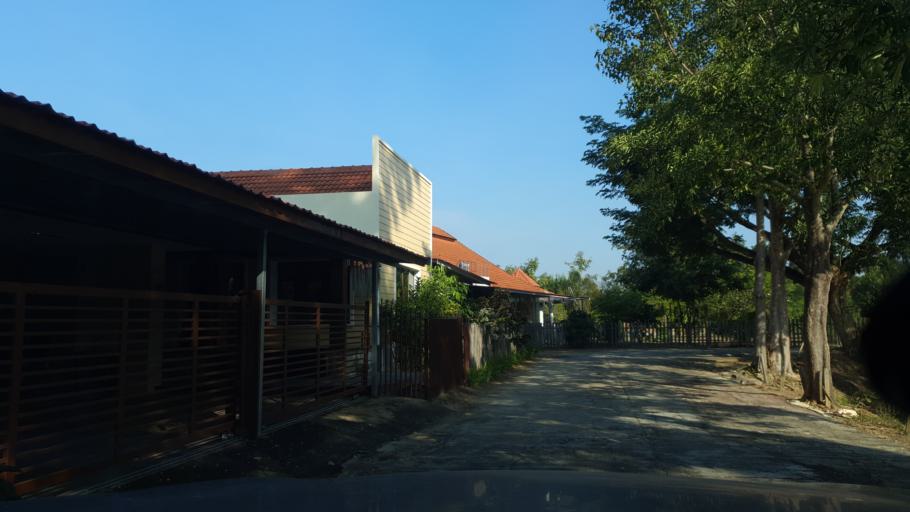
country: TH
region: Chiang Mai
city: Saraphi
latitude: 18.7136
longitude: 98.9961
